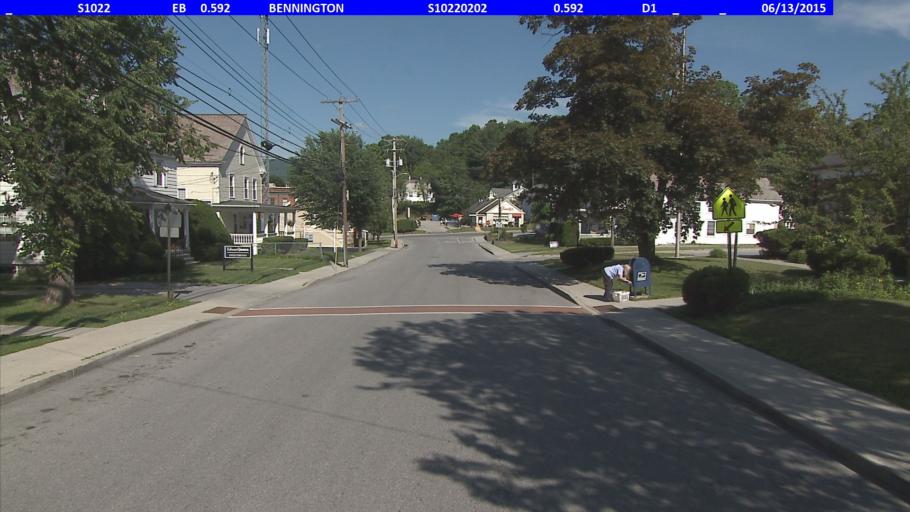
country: US
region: Vermont
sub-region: Bennington County
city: Bennington
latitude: 42.8768
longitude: -73.1985
